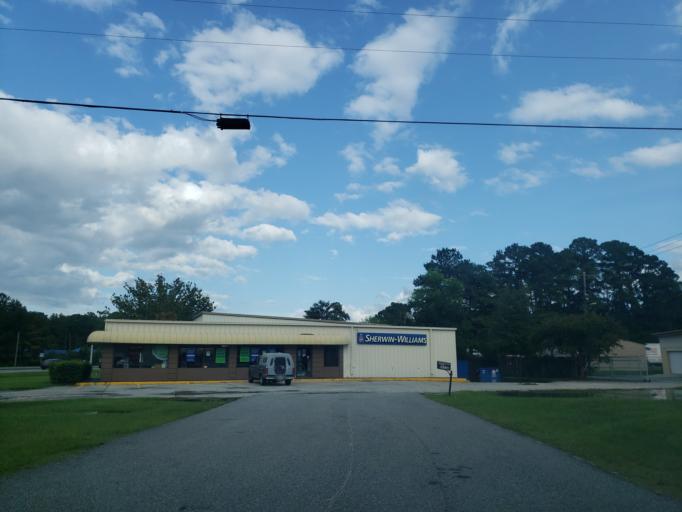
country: US
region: Georgia
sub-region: Chatham County
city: Georgetown
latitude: 31.9965
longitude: -81.2626
